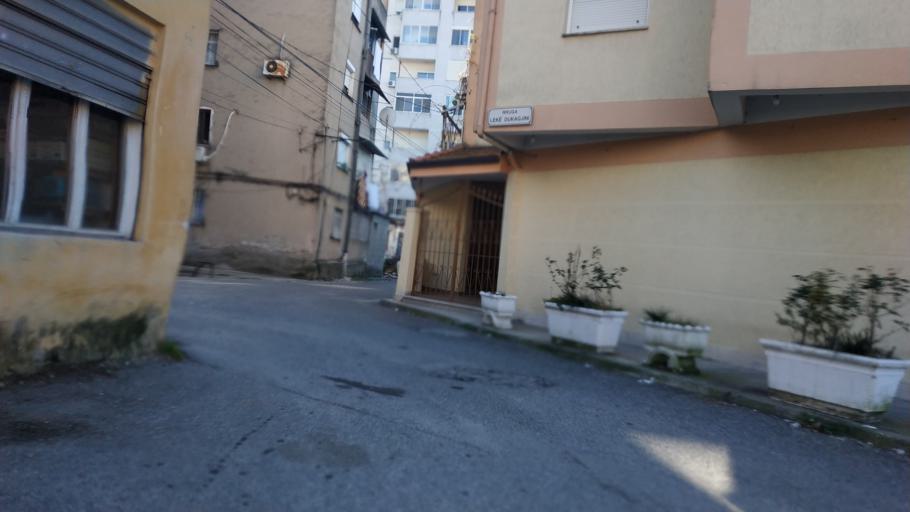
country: AL
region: Shkoder
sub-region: Rrethi i Shkodres
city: Shkoder
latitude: 42.0732
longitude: 19.5146
